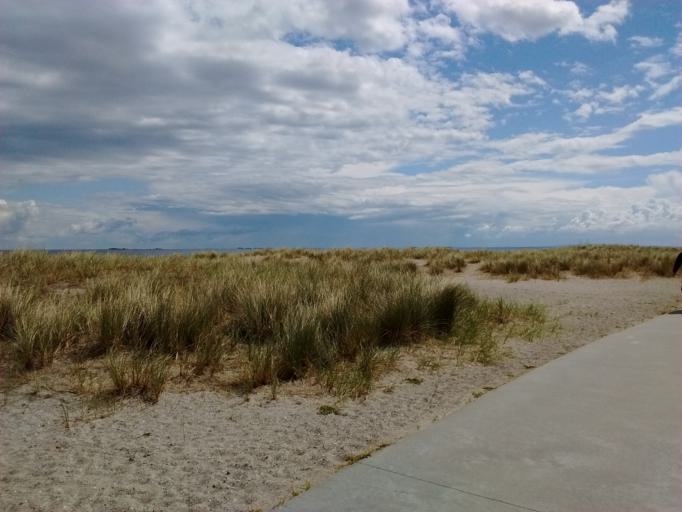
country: DK
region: Capital Region
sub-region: Kobenhavn
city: Christianshavn
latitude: 55.6613
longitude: 12.6393
